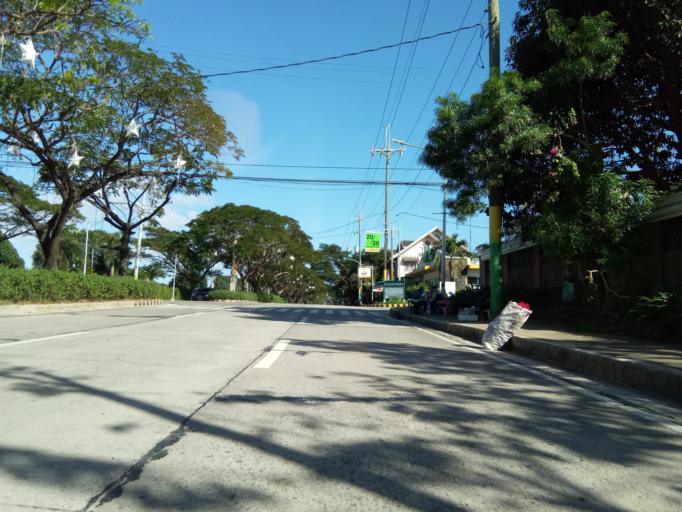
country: PH
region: Calabarzon
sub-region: Province of Cavite
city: Dasmarinas
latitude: 14.3506
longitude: 120.9611
